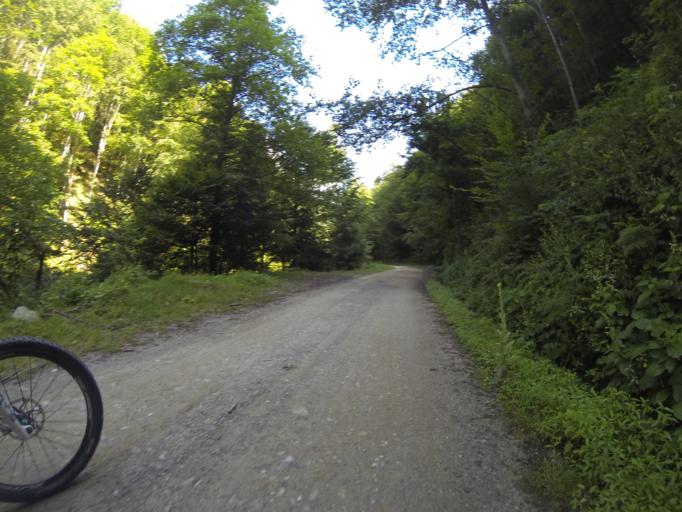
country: RO
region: Valcea
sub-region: Comuna Costesti
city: Bistrita
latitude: 45.2220
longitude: 24.0037
